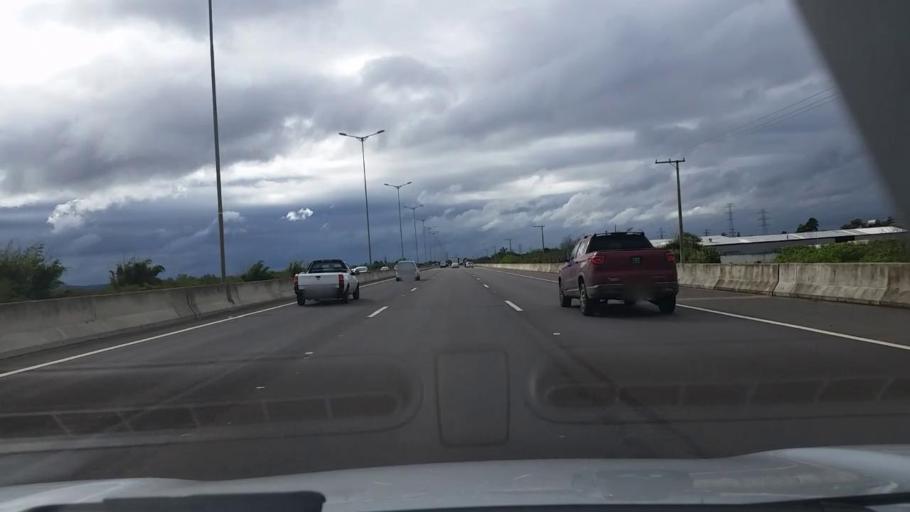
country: BR
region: Rio Grande do Sul
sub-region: Canoas
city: Canoas
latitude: -29.9510
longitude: -51.2032
